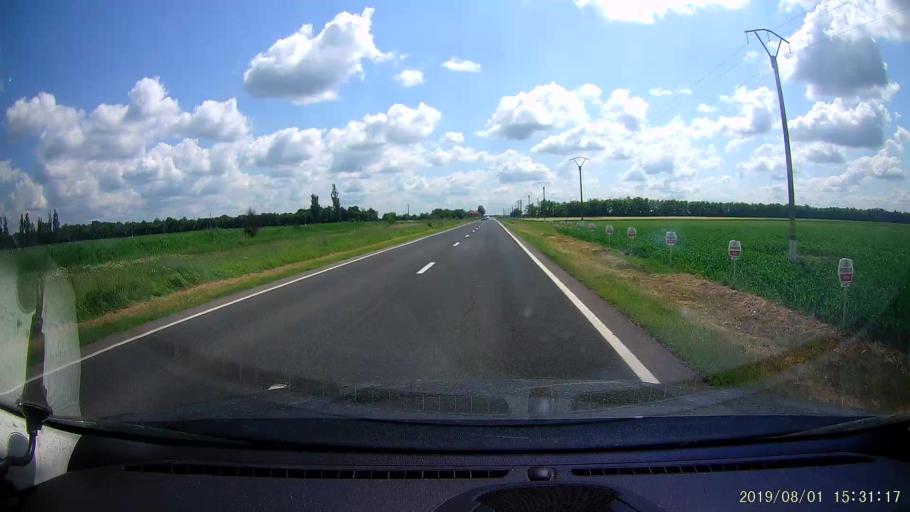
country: RO
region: Braila
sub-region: Comuna Insuratei
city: Insuratei
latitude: 44.9479
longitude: 27.6614
